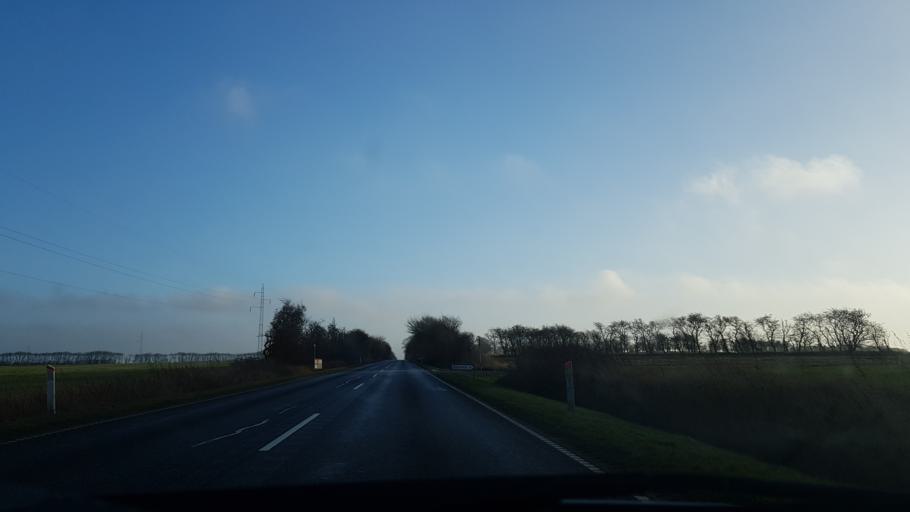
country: DK
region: South Denmark
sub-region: Haderslev Kommune
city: Vojens
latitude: 55.1901
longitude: 9.2148
